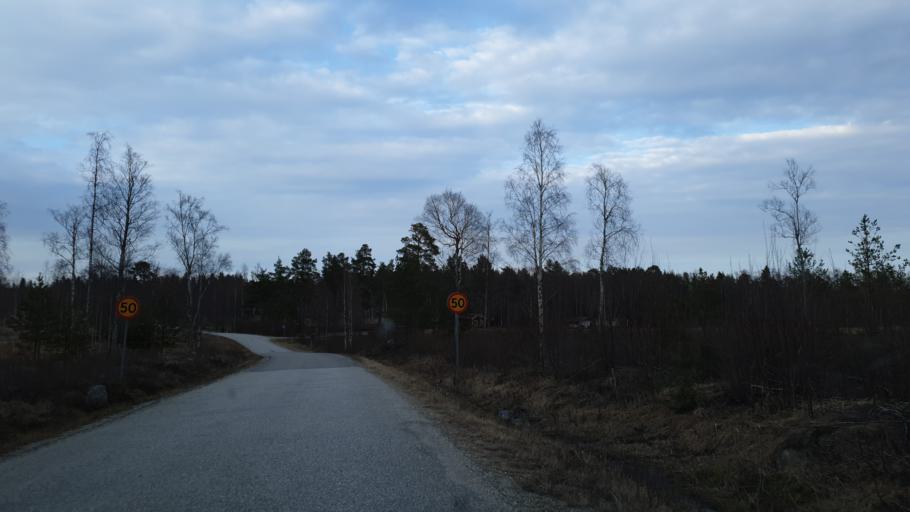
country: SE
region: Vaesternorrland
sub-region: Sundsvalls Kommun
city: Njurundabommen
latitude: 62.0178
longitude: 17.4050
